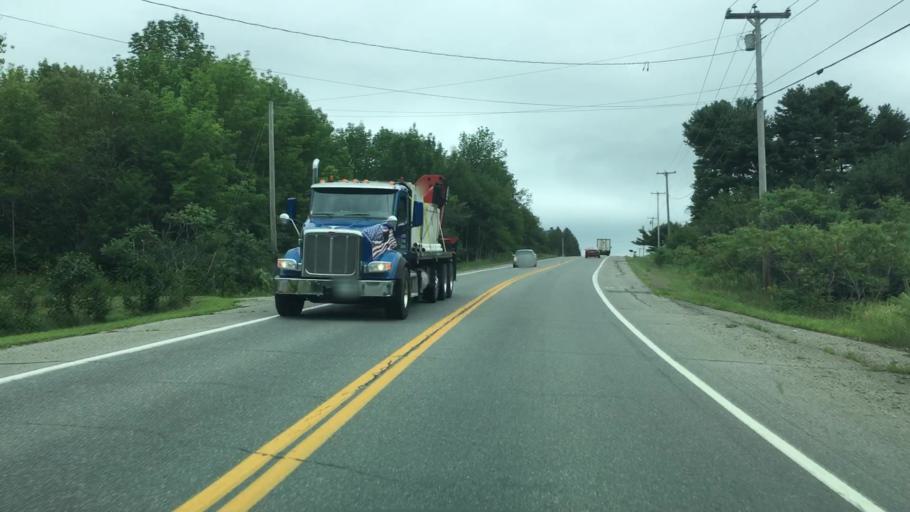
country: US
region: Maine
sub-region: Waldo County
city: Frankfort
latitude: 44.5590
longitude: -68.8662
